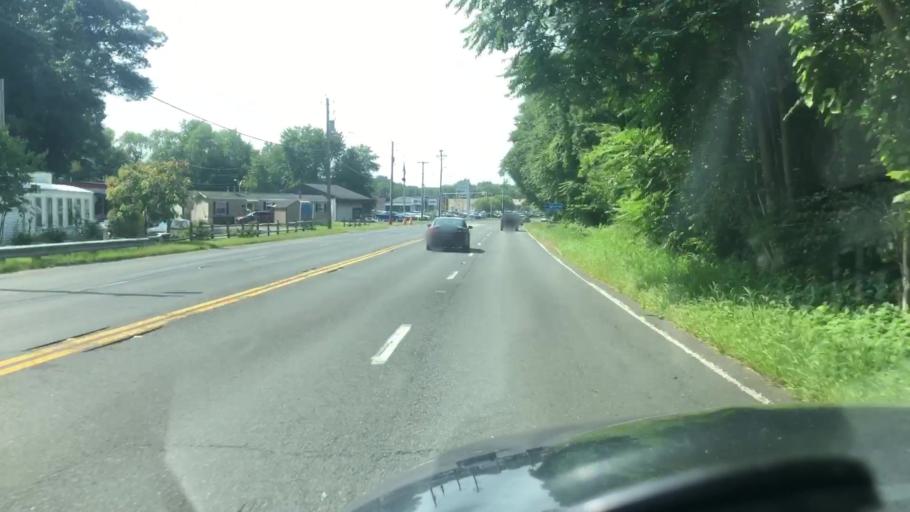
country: US
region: Massachusetts
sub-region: Hampden County
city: Westfield
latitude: 42.1074
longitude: -72.7019
